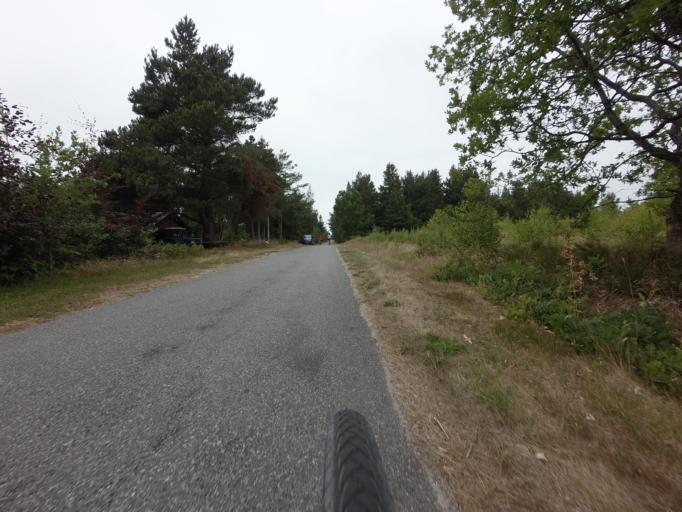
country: DK
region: North Denmark
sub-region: Laeso Kommune
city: Byrum
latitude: 57.2773
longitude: 10.9618
